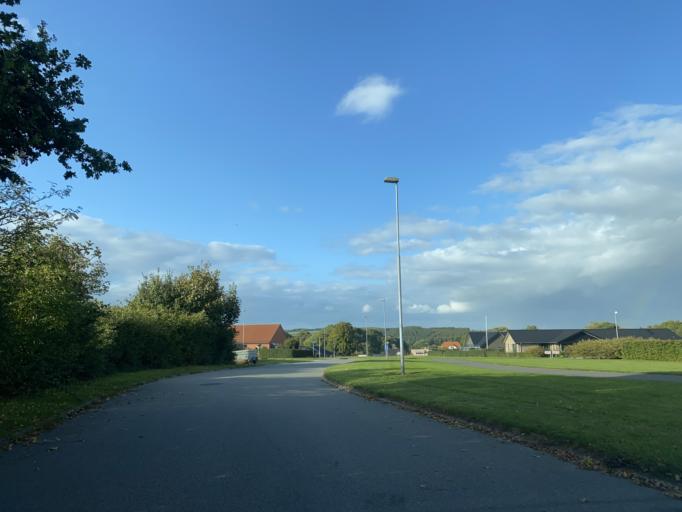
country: DK
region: Central Jutland
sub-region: Skanderborg Kommune
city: Ry
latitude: 56.1538
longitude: 9.8114
